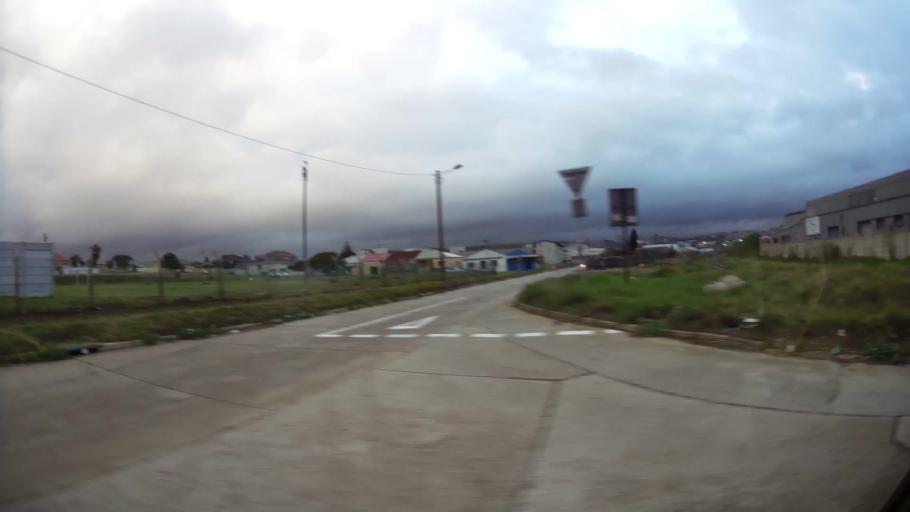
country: ZA
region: Eastern Cape
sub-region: Nelson Mandela Bay Metropolitan Municipality
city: Port Elizabeth
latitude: -33.9281
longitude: 25.5958
